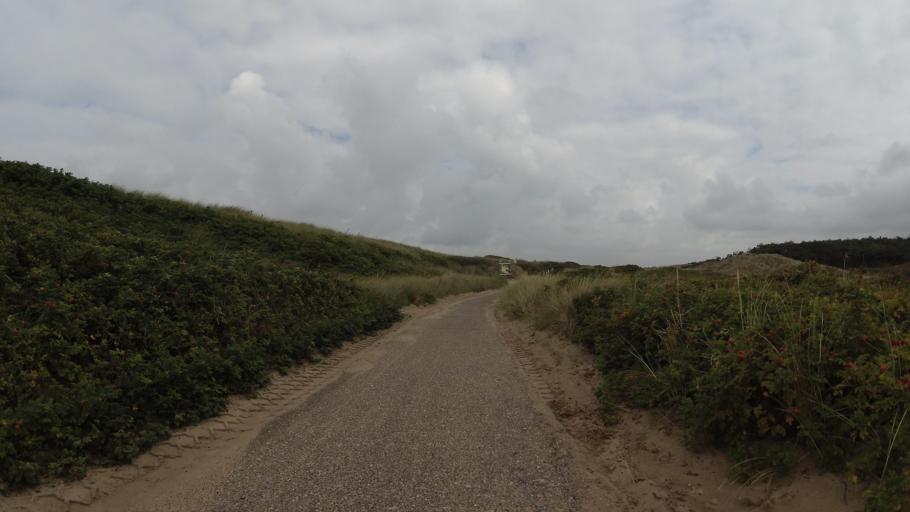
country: NL
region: North Holland
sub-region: Gemeente Den Helder
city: Den Helder
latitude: 52.9369
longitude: 4.7174
